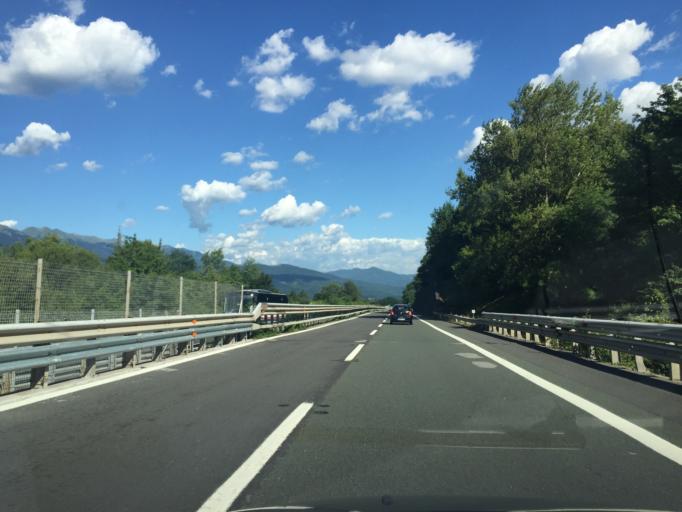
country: IT
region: Tuscany
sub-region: Provincia di Massa-Carrara
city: Pontremoli
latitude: 44.3778
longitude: 9.8572
